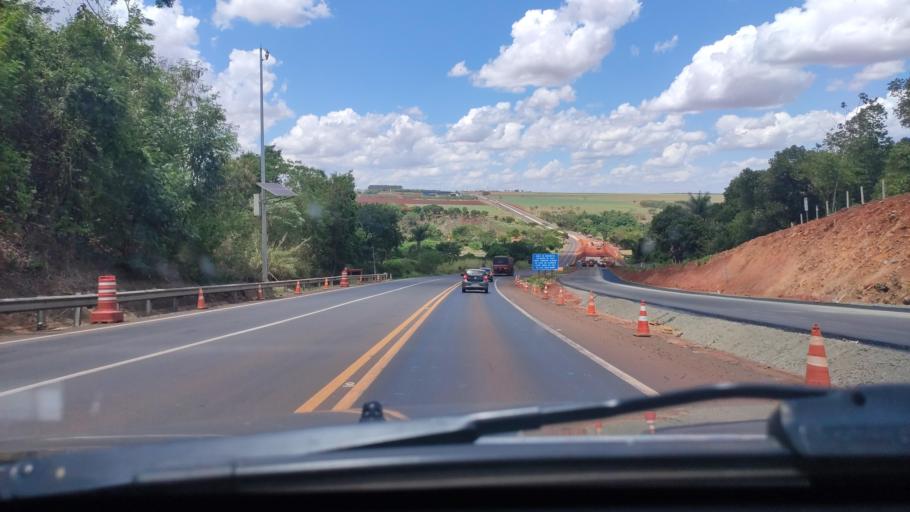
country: BR
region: Sao Paulo
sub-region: Jau
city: Jau
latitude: -22.2296
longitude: -48.5294
